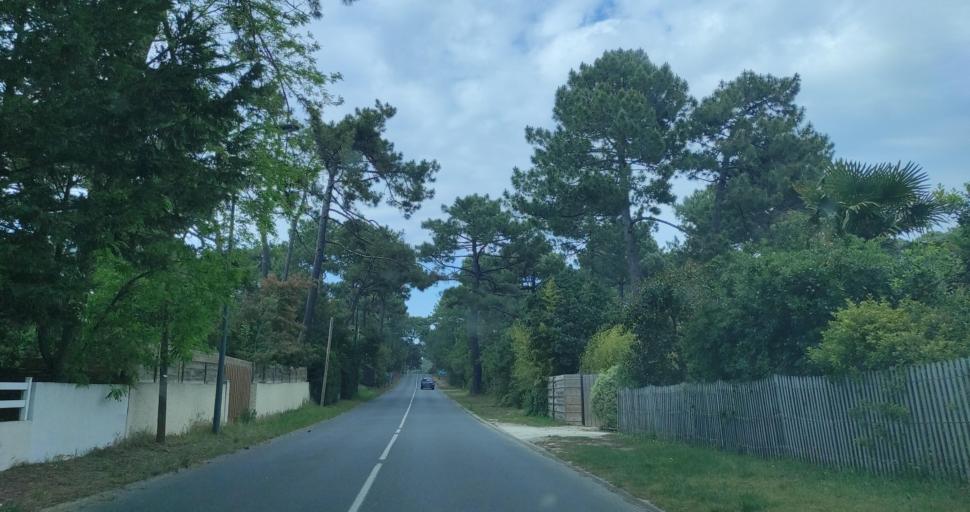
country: FR
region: Aquitaine
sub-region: Departement de la Gironde
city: Arcachon
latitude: 44.6632
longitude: -1.2434
